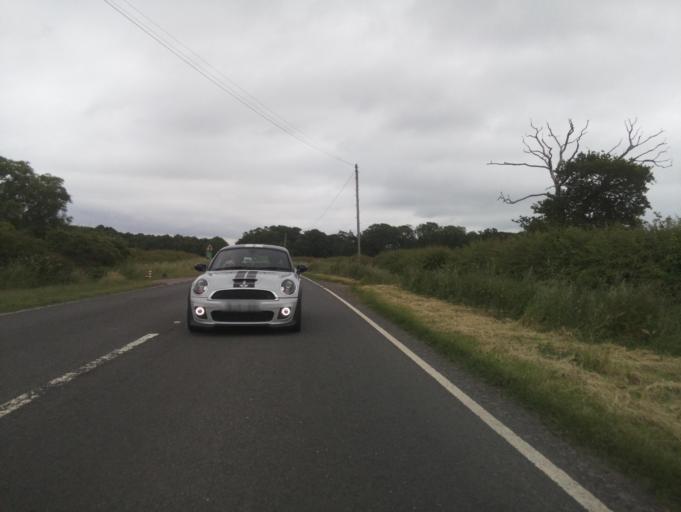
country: GB
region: England
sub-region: Nottinghamshire
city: East Leake
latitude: 52.8140
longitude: -1.1871
